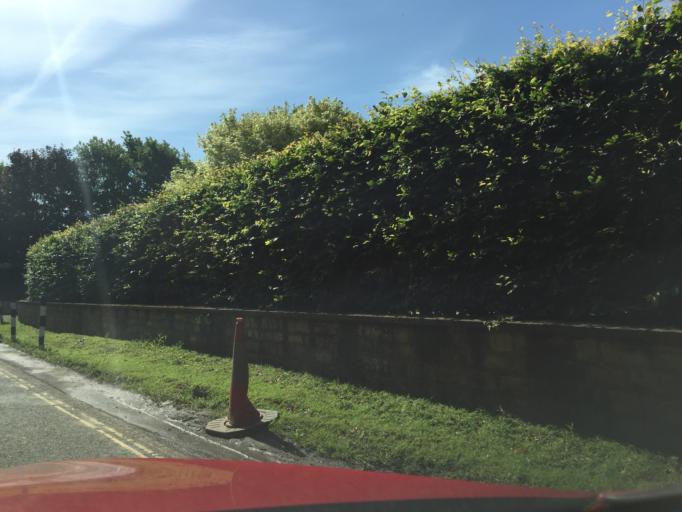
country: GB
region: England
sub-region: Gloucestershire
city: Stonehouse
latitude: 51.7942
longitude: -2.3237
